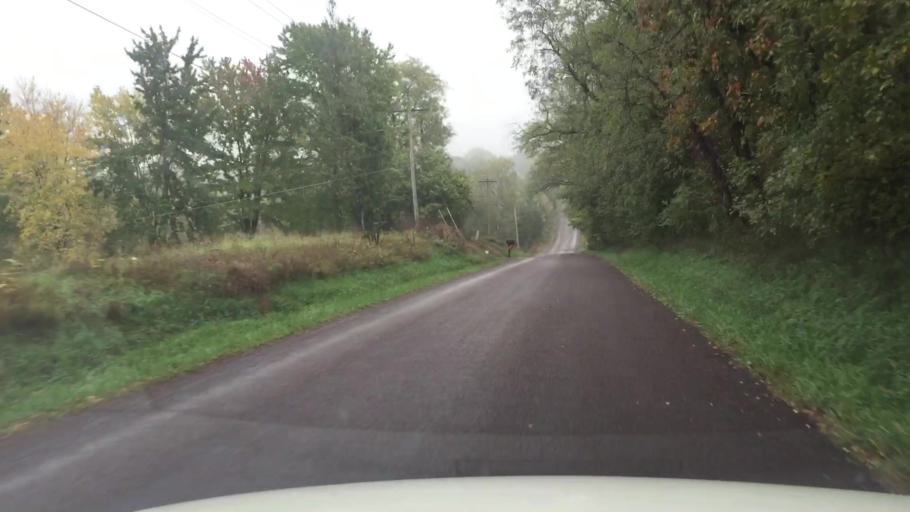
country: US
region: Missouri
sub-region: Boone County
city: Columbia
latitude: 38.8559
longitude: -92.3574
